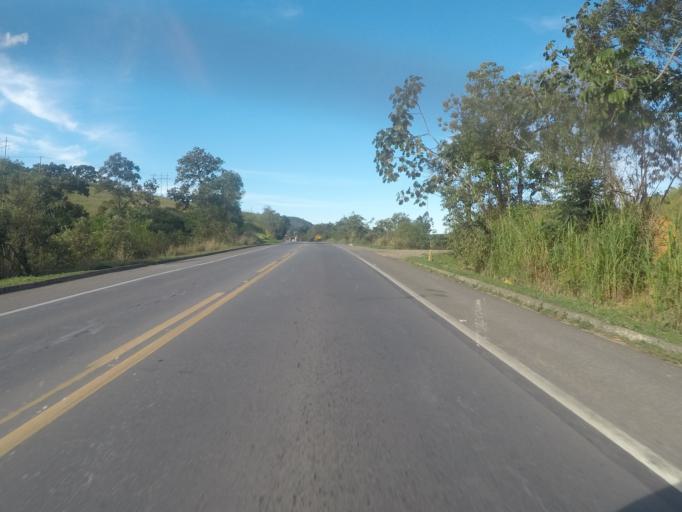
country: BR
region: Espirito Santo
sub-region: Ibiracu
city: Ibiracu
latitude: -19.8665
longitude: -40.3984
